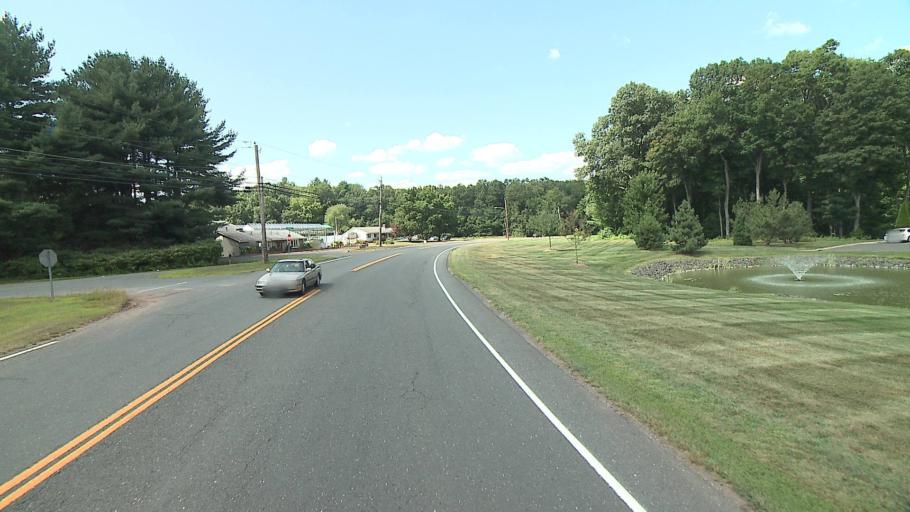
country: US
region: Connecticut
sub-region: Hartford County
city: Broad Brook
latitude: 41.9335
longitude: -72.5597
